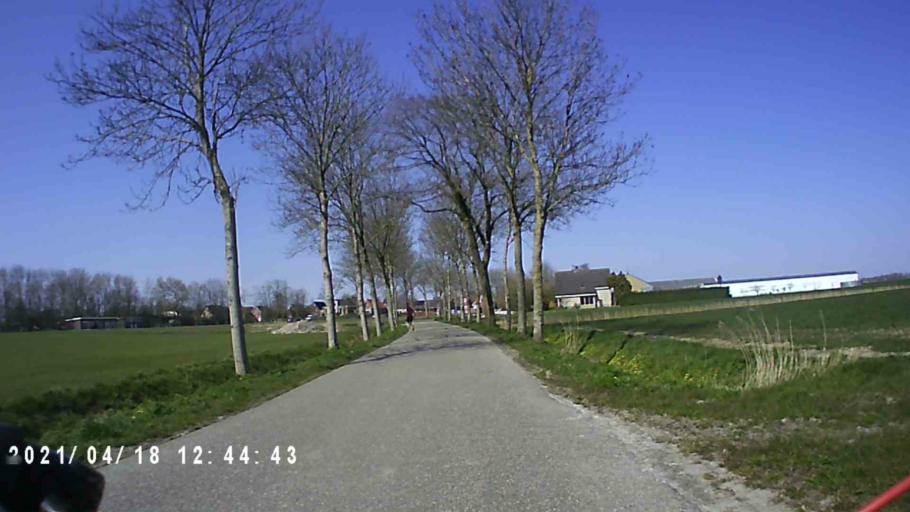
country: NL
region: Friesland
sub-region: Gemeente Dantumadiel
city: Walterswald
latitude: 53.3635
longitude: 6.0540
